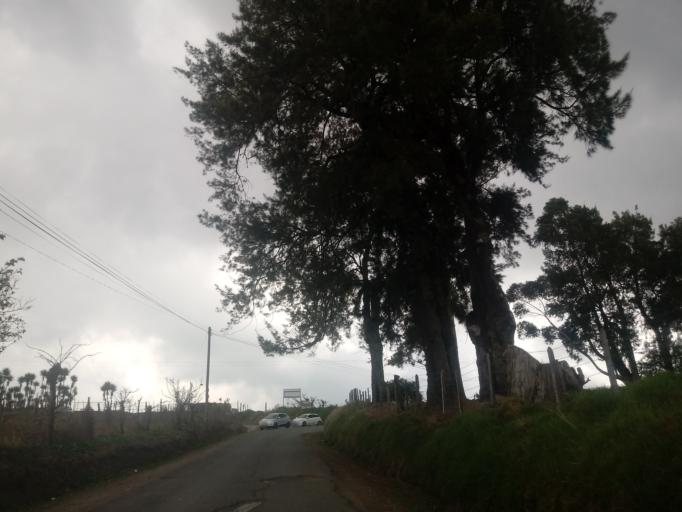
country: CR
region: Cartago
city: Cot
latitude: 9.9310
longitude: -83.8841
